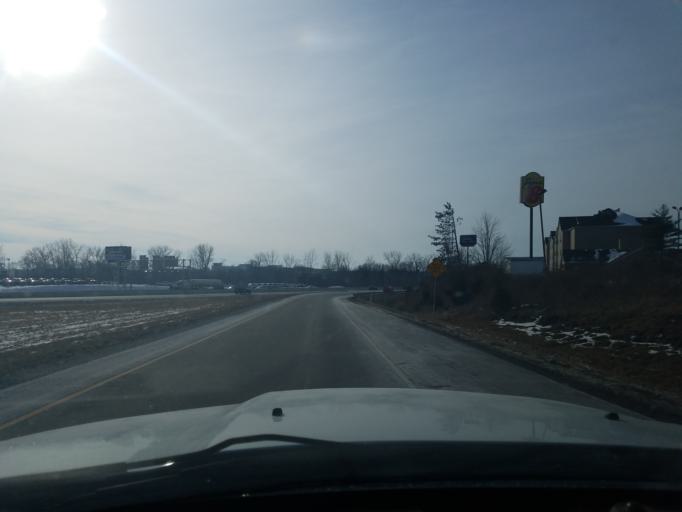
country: US
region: Indiana
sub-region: Allen County
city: Fort Wayne
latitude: 41.1302
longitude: -85.1615
